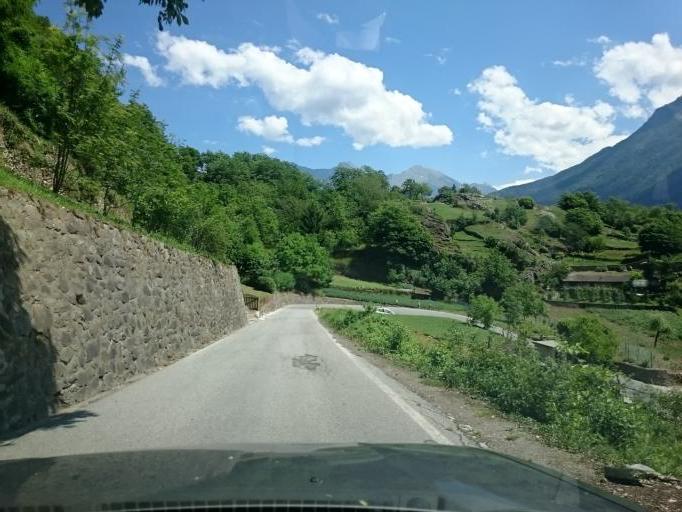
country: IT
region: Lombardy
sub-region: Provincia di Brescia
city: Capo di Ponte
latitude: 46.0369
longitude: 10.3371
